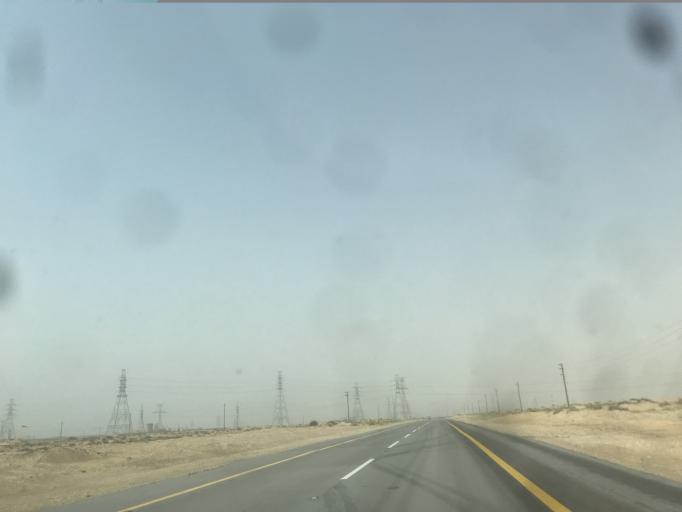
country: SA
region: Eastern Province
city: Abqaiq
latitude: 25.9367
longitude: 49.7246
